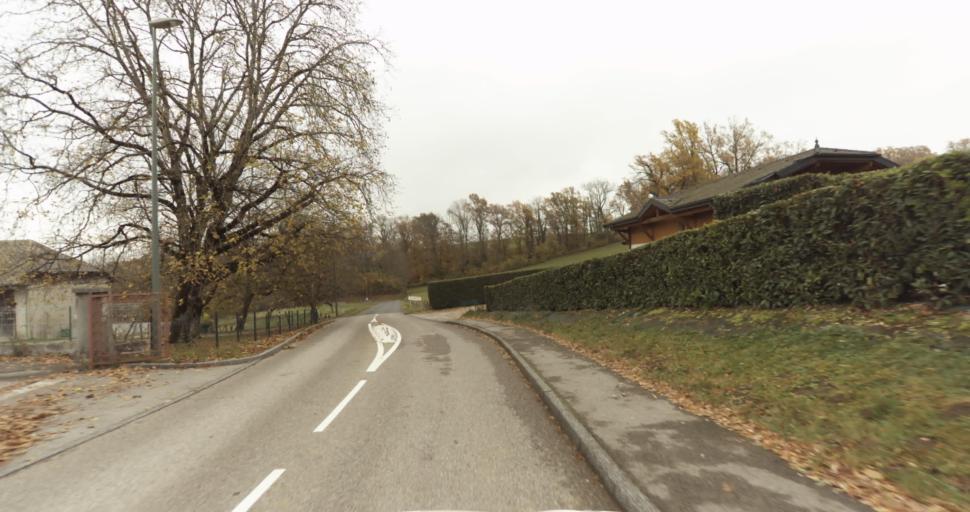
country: FR
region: Rhone-Alpes
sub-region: Departement de la Haute-Savoie
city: Alby-sur-Cheran
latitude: 45.8086
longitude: 6.0061
